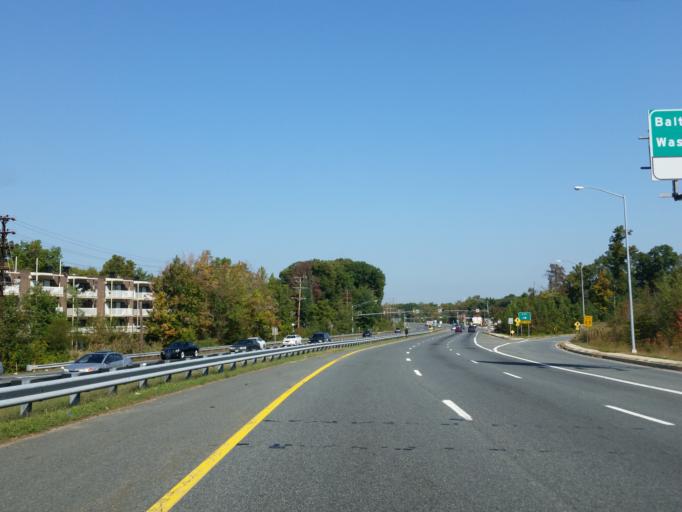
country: US
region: Maryland
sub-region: Prince George's County
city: South Laurel
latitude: 39.0602
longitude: -76.8392
